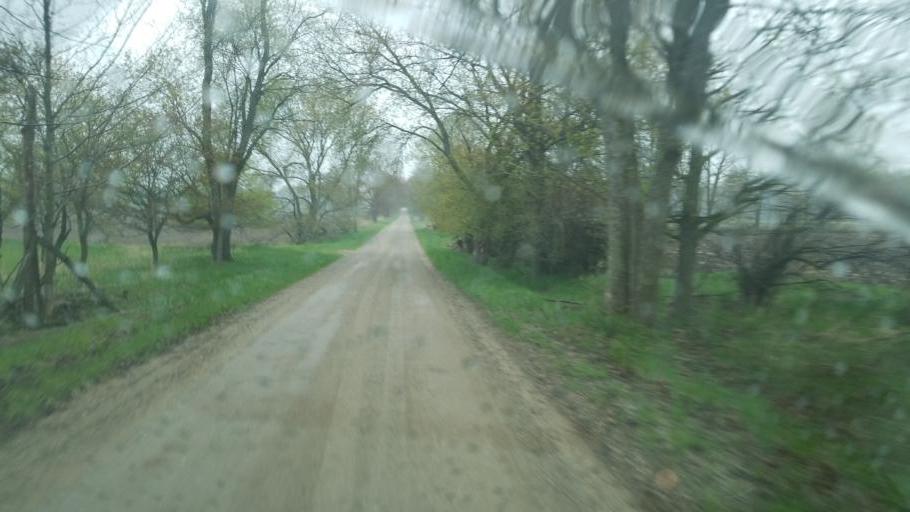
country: US
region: Michigan
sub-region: Mecosta County
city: Canadian Lakes
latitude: 43.5127
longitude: -85.3139
